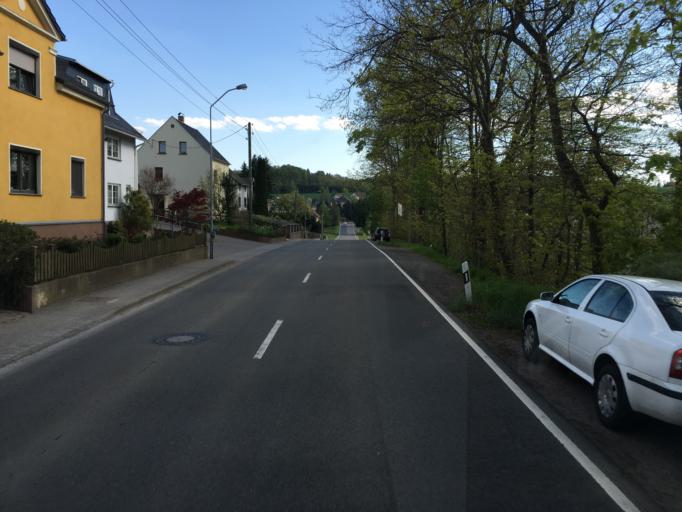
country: DE
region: Saxony
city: Rosswein
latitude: 51.0344
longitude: 13.1593
